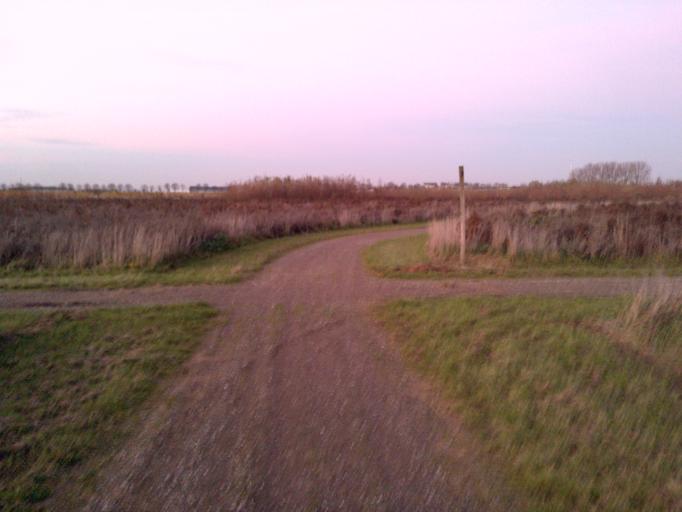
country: NL
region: South Holland
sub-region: Gemeente Waddinxveen
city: Groenswaard
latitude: 52.0704
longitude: 4.6203
